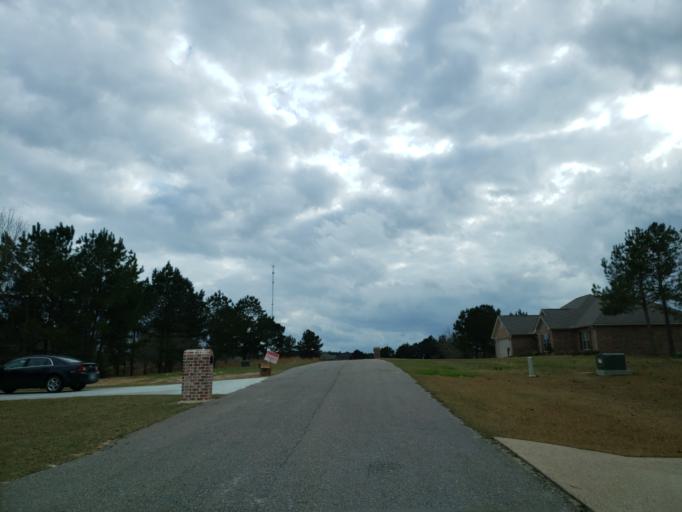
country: US
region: Mississippi
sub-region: Jones County
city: Ellisville
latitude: 31.5557
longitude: -89.2535
